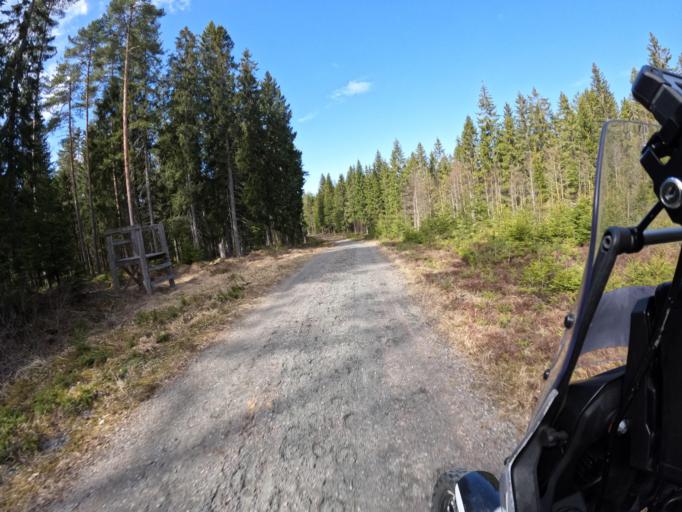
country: SE
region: Joenkoeping
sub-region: Mullsjo Kommun
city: Mullsjoe
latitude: 57.9456
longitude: 13.6902
